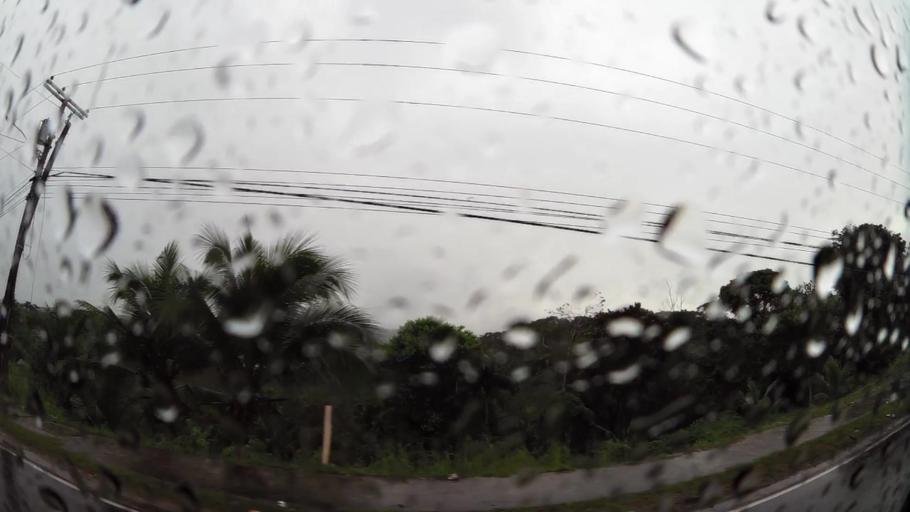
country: PA
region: Colon
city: Puerto Pilon
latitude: 9.3573
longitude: -79.8007
